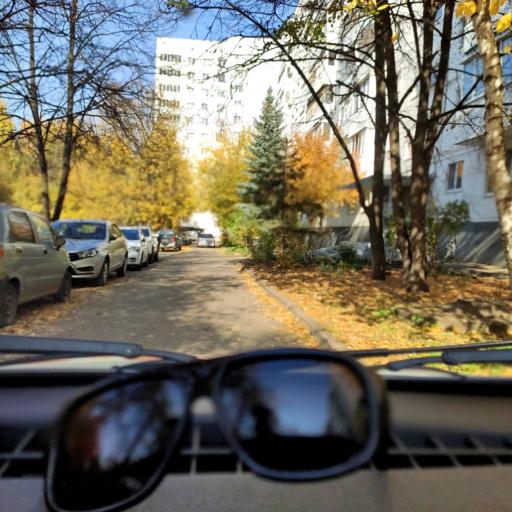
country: RU
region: Bashkortostan
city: Ufa
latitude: 54.7480
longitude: 56.0295
